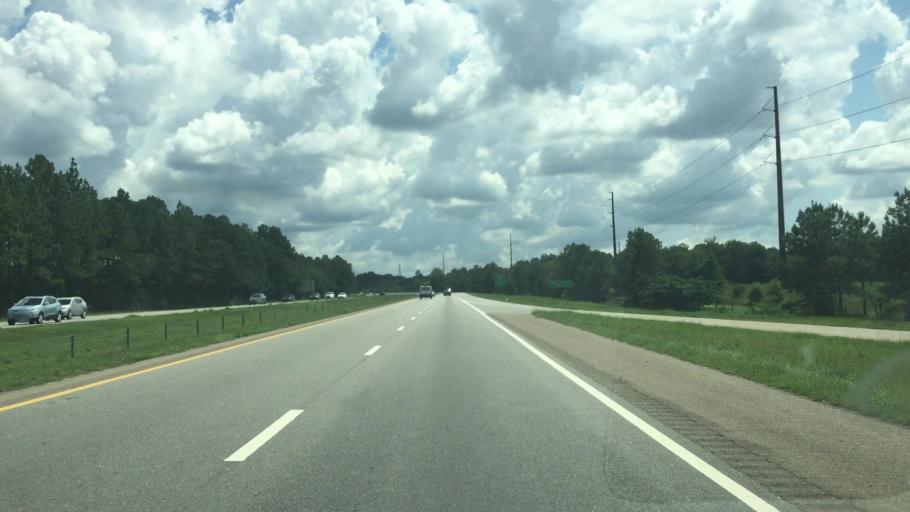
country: US
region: North Carolina
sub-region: Richmond County
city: Hamlet
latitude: 34.8561
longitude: -79.6923
